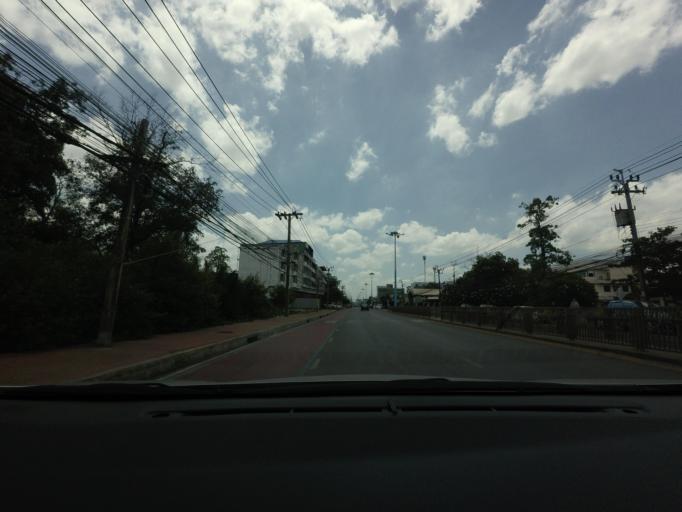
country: TH
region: Samut Prakan
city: Samut Prakan
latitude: 13.5673
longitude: 100.5908
